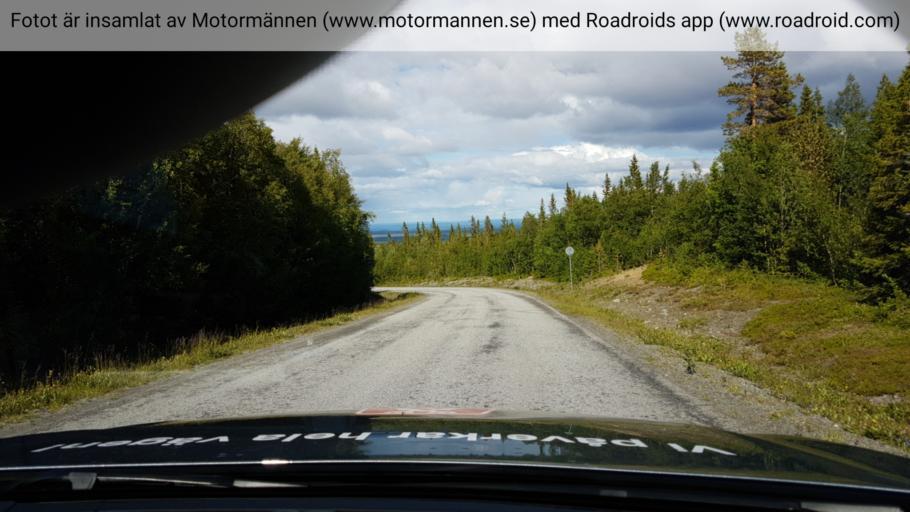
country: SE
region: Jaemtland
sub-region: Krokoms Kommun
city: Valla
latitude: 63.0283
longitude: 13.9484
